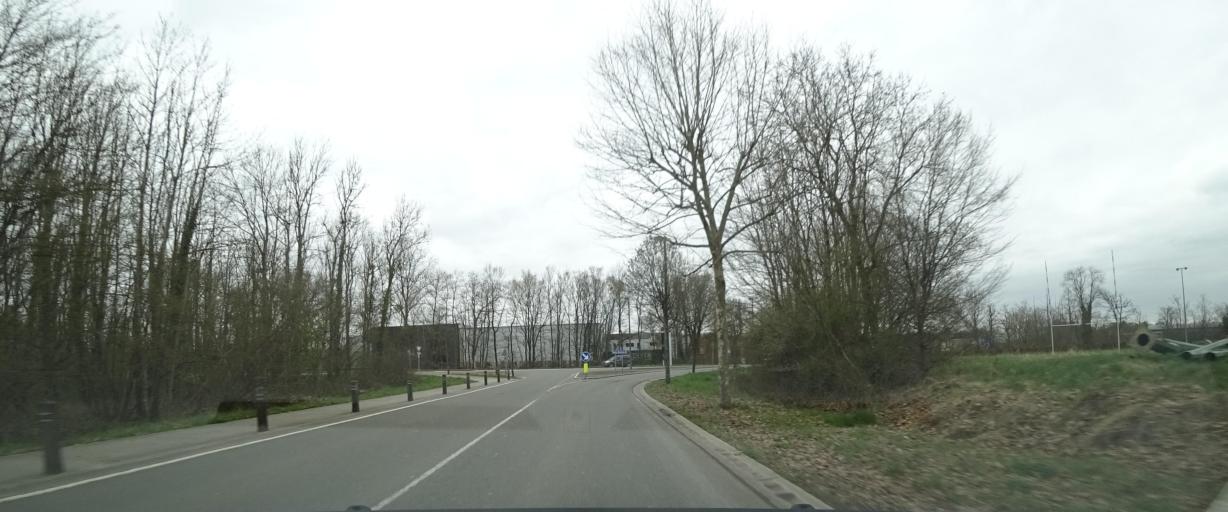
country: BE
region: Wallonia
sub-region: Province du Luxembourg
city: Marche-en-Famenne
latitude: 50.2205
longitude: 5.3339
